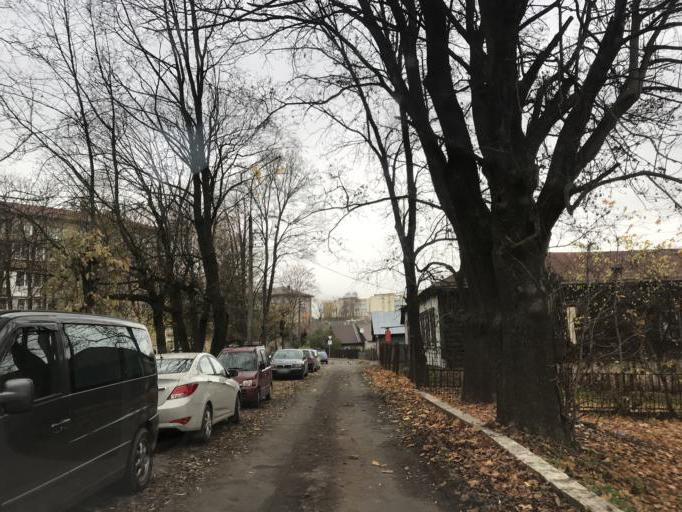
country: BY
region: Mogilev
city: Mahilyow
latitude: 53.9015
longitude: 30.3467
